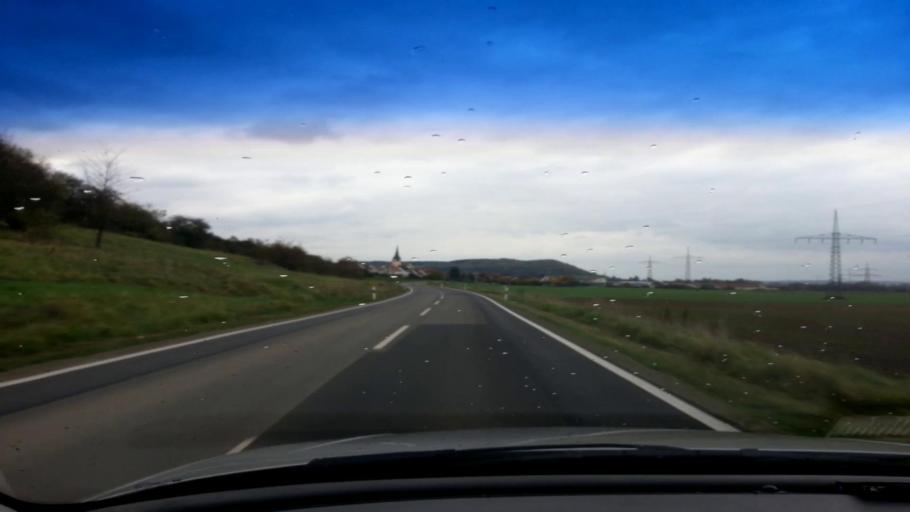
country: DE
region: Bavaria
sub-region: Regierungsbezirk Unterfranken
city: Stettfeld
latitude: 49.9748
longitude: 10.7111
